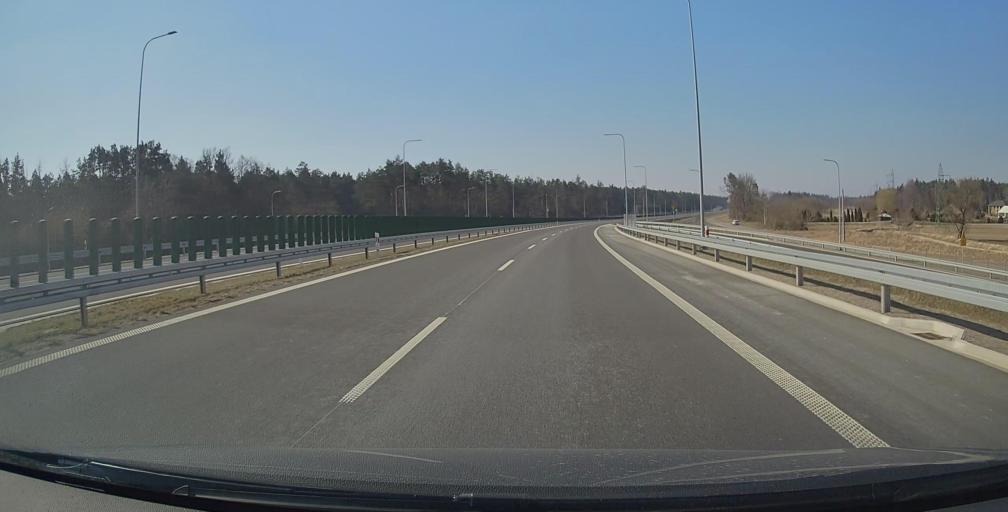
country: PL
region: Lublin Voivodeship
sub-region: Powiat janowski
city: Janow Lubelski
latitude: 50.6929
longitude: 22.3736
